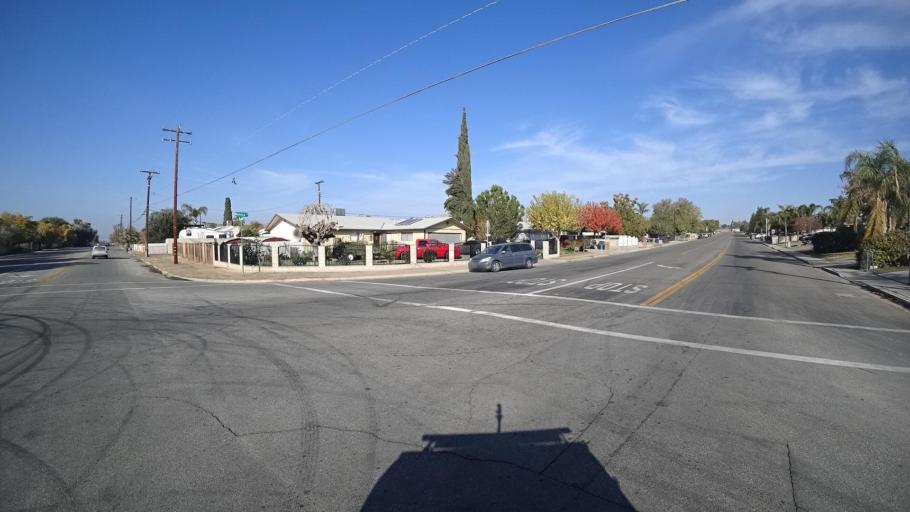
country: US
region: California
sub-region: Kern County
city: Lamont
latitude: 35.3691
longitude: -118.9052
